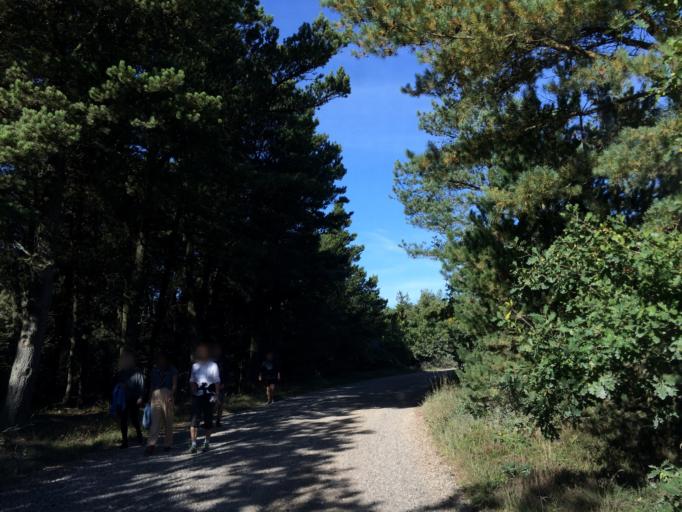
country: DK
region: Central Jutland
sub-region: Holstebro Kommune
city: Ulfborg
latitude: 56.2848
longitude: 8.1485
